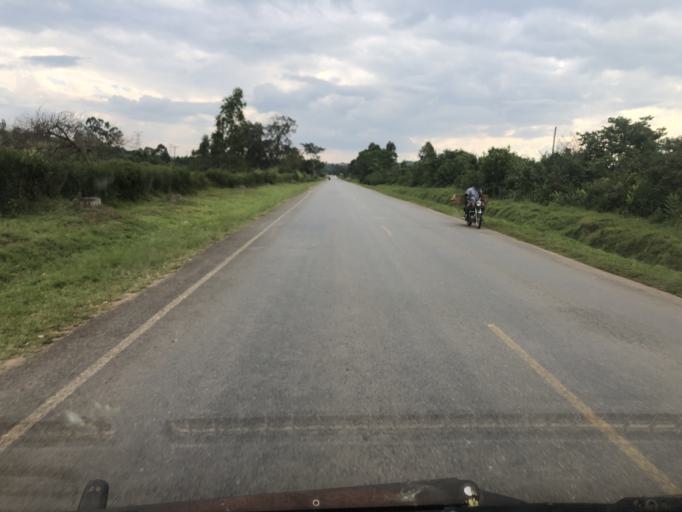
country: UG
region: Western Region
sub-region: Sheema District
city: Kibingo
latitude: -0.5799
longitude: 30.4299
